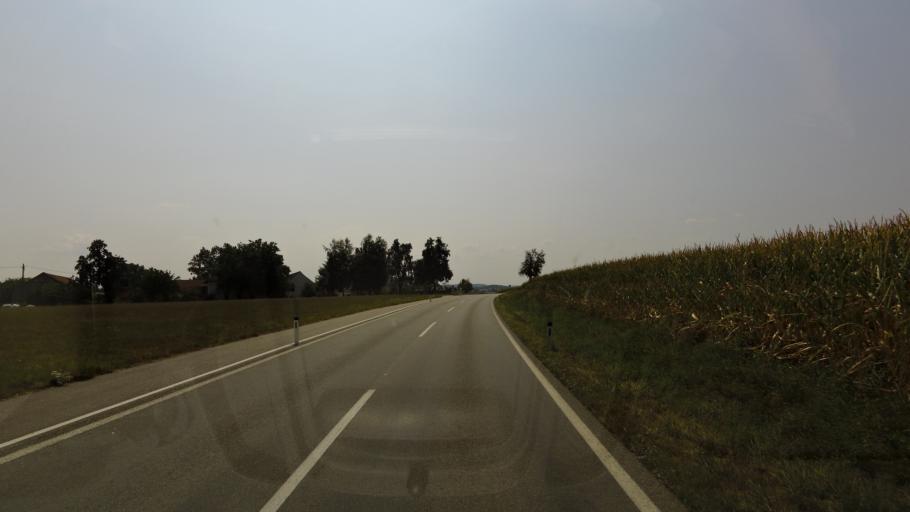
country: DE
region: Bavaria
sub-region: Lower Bavaria
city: Bad Fussing
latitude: 48.3087
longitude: 13.3287
